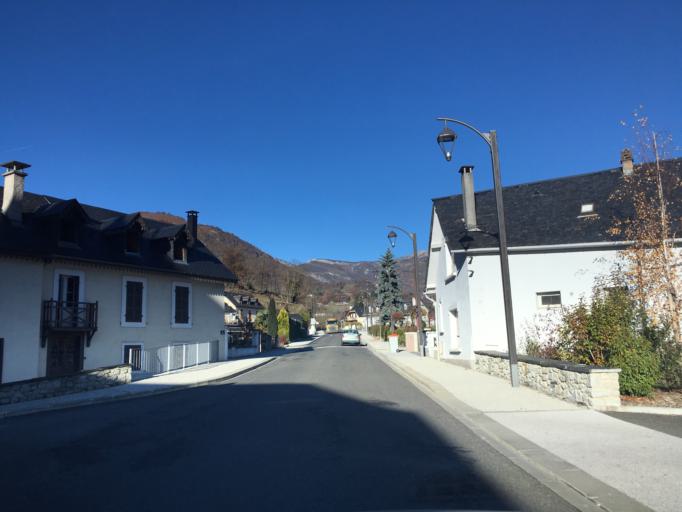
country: FR
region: Midi-Pyrenees
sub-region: Departement des Hautes-Pyrenees
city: Argeles-Gazost
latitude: 42.9969
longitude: -0.0926
